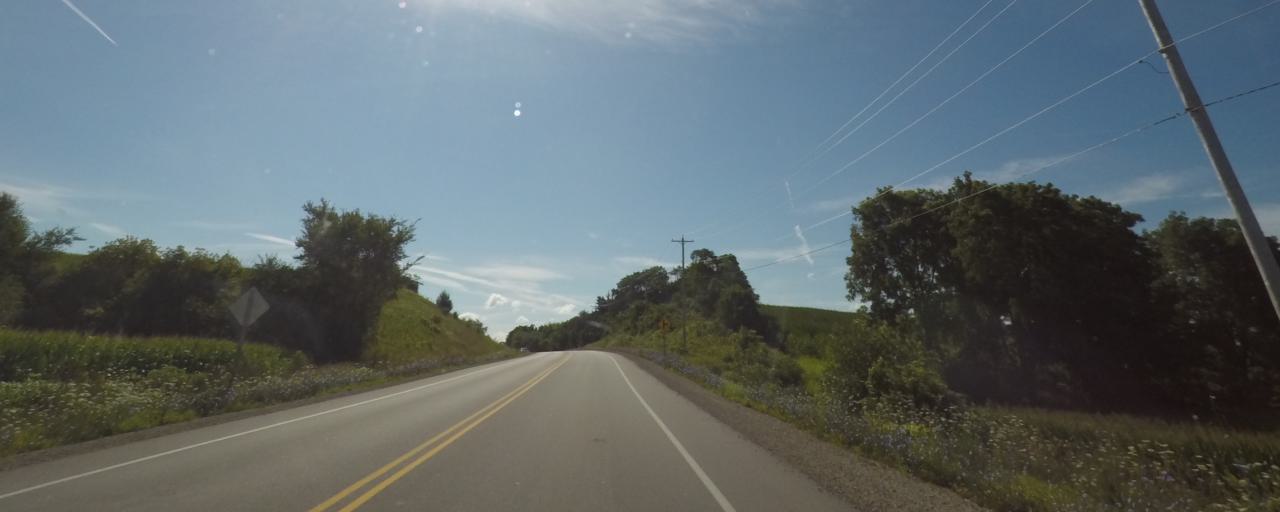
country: US
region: Wisconsin
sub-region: Jefferson County
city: Johnson Creek
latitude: 43.0742
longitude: -88.7107
